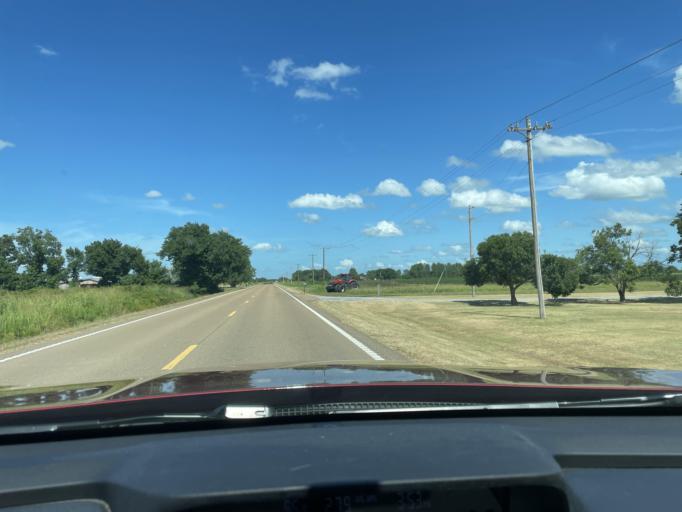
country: US
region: Mississippi
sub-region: Washington County
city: Hollandale
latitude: 33.1843
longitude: -90.6727
